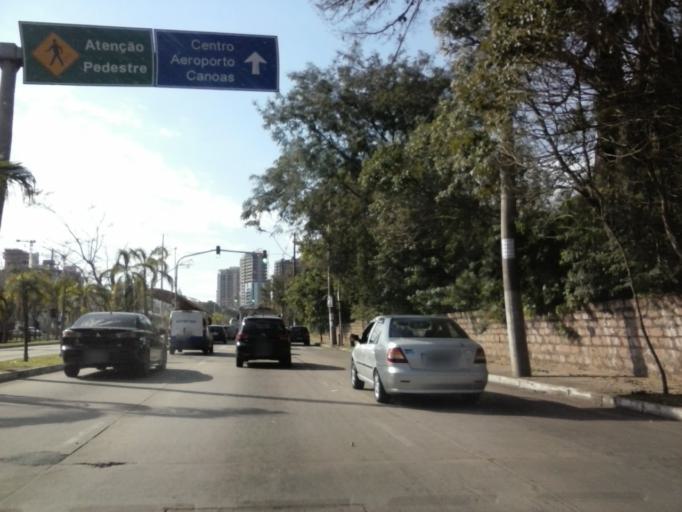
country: BR
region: Rio Grande do Sul
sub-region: Porto Alegre
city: Porto Alegre
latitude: -30.0486
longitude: -51.1789
